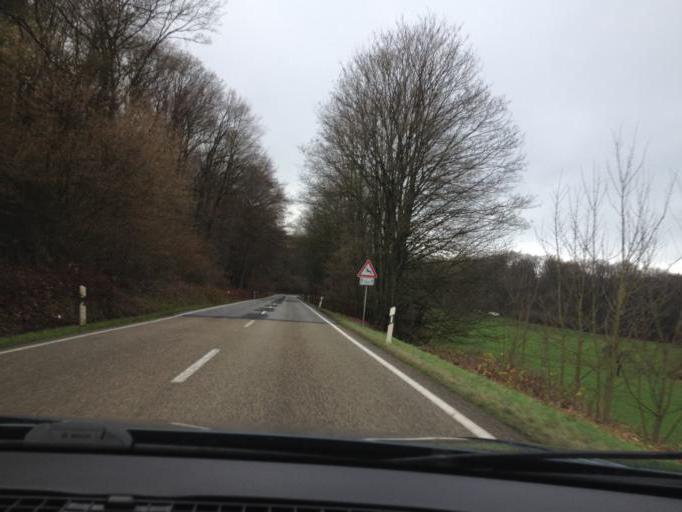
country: DE
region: Saarland
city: Sankt Wendel
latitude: 49.4513
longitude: 7.2151
